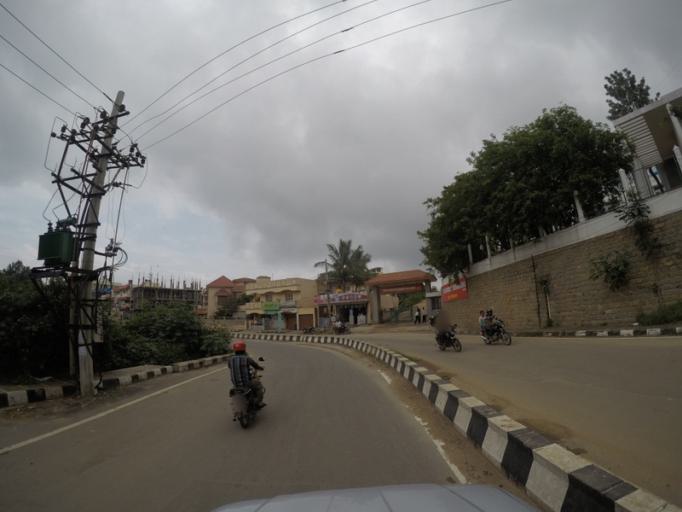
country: IN
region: Karnataka
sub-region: Bangalore Urban
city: Yelahanka
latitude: 13.0855
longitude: 77.5486
